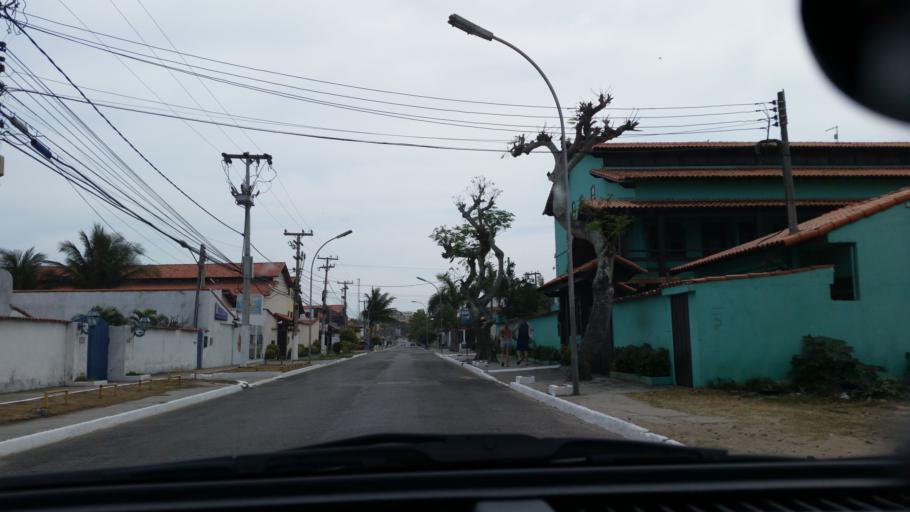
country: BR
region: Rio de Janeiro
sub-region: Cabo Frio
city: Cabo Frio
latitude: -22.8644
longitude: -41.9891
